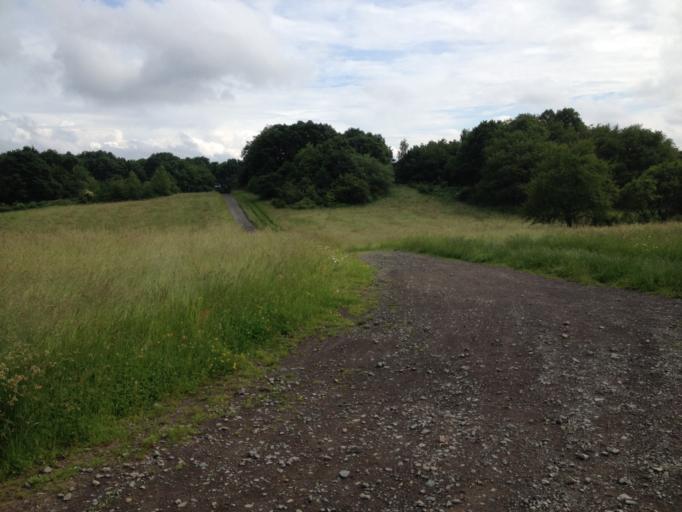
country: DE
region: Saarland
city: Hangard
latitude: 49.4010
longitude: 7.1932
